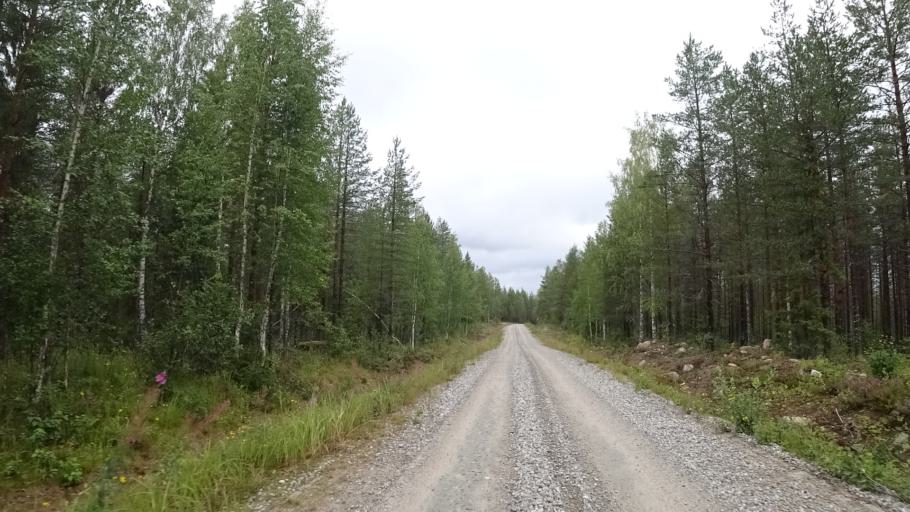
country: FI
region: North Karelia
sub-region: Pielisen Karjala
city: Lieksa
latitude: 63.4763
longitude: 30.2611
